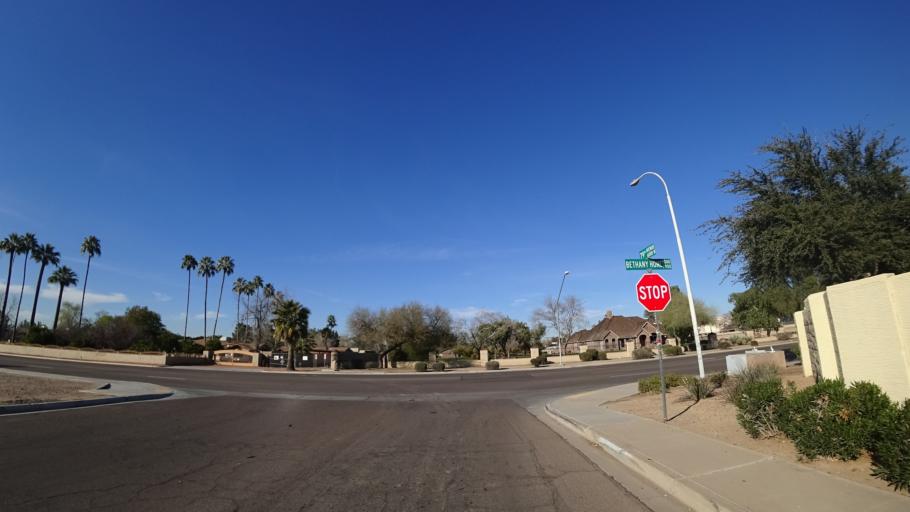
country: US
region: Arizona
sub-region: Maricopa County
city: Glendale
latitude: 33.5231
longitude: -112.2290
